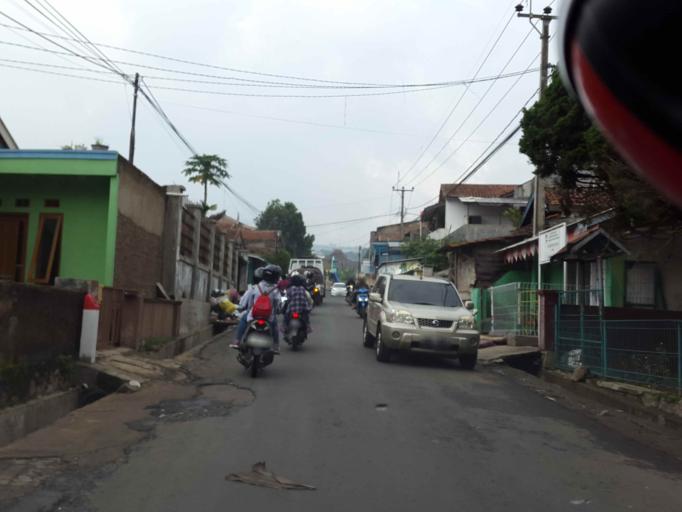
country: ID
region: West Java
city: Cimahi
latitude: -6.8436
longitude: 107.5721
